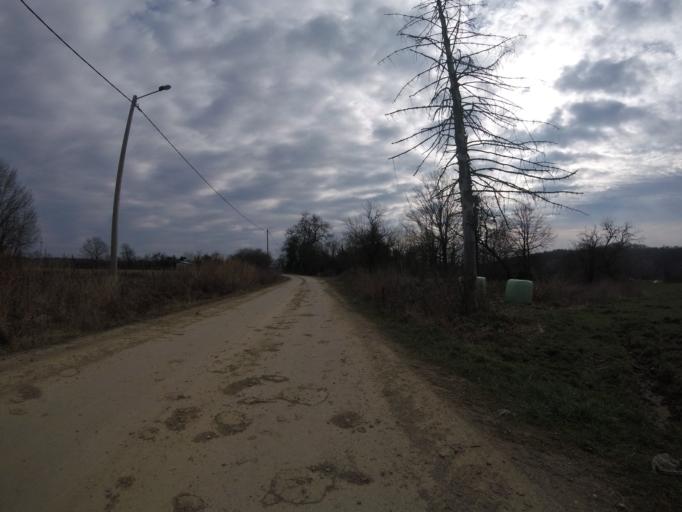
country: HR
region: Sisacko-Moslavacka
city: Glina
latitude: 45.4624
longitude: 16.0464
